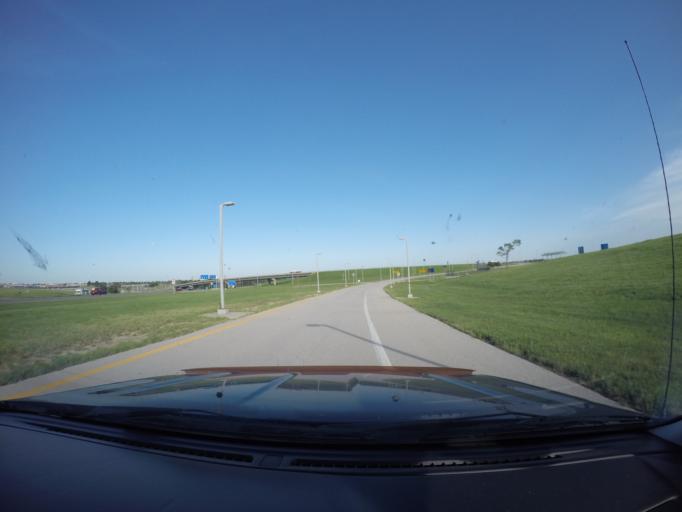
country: US
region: Missouri
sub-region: Platte County
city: Weatherby Lake
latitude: 39.3116
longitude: -94.6988
